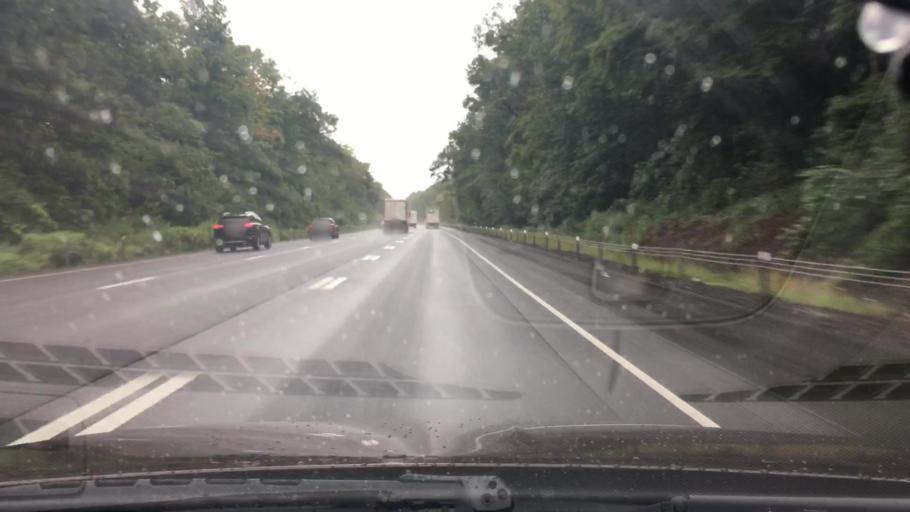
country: US
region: Connecticut
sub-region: New Haven County
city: Southbury
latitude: 41.4810
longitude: -73.1966
